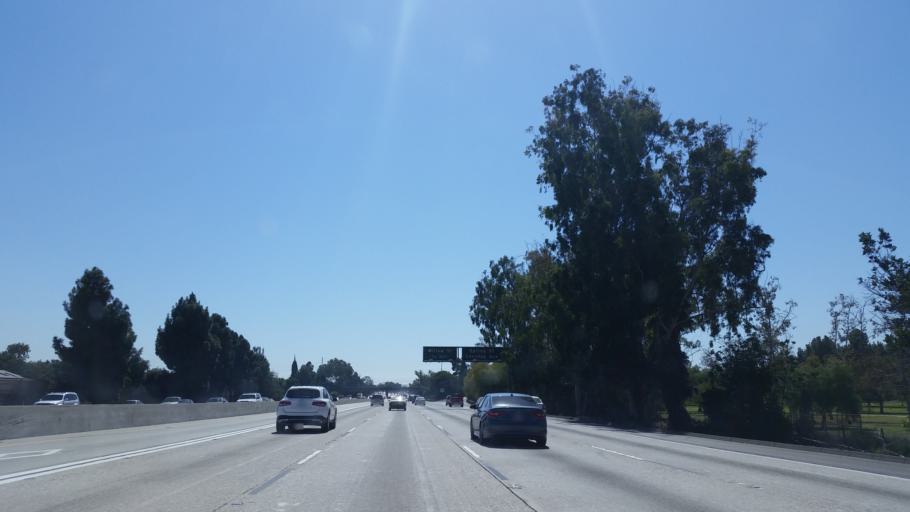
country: US
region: California
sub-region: Orange County
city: Los Alamitos
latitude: 33.8155
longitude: -118.0816
